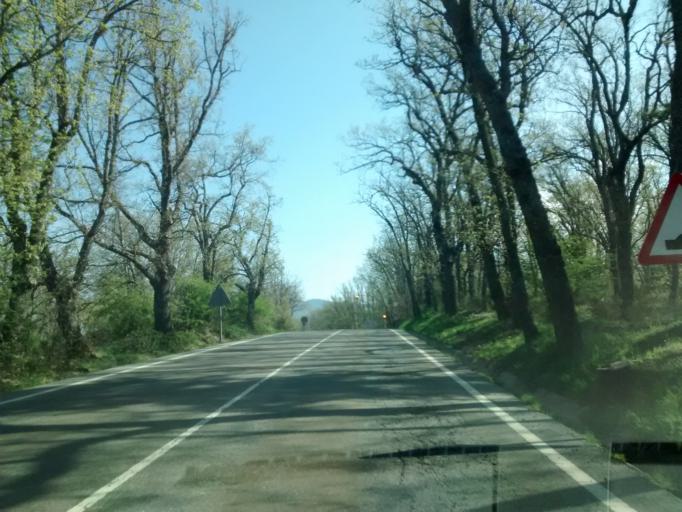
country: ES
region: Castille and Leon
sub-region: Provincia de Segovia
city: San Ildefonso
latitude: 40.8710
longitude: -4.0221
